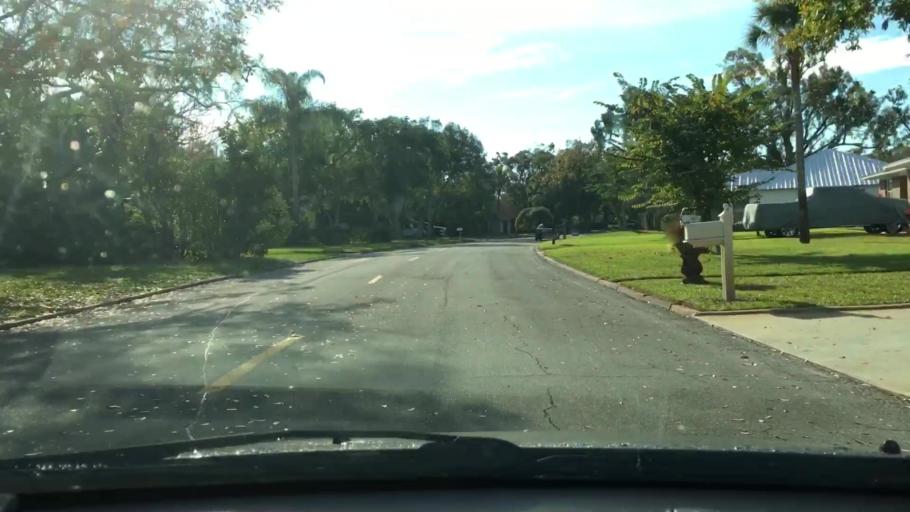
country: US
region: Florida
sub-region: Indian River County
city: Vero Beach
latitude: 27.6435
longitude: -80.4073
